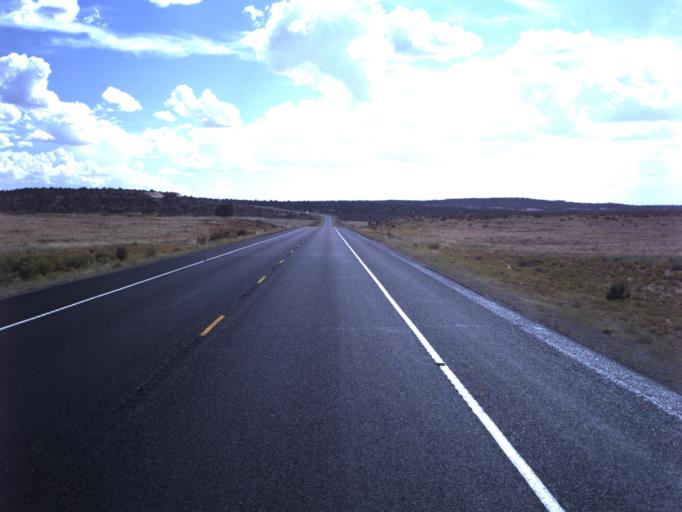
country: US
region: Utah
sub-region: Grand County
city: Moab
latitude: 38.6234
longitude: -109.8105
